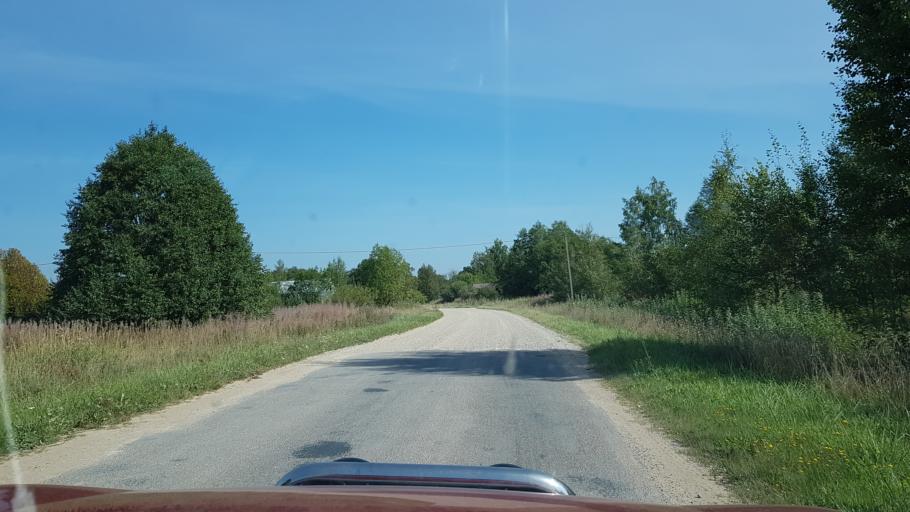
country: EE
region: Viljandimaa
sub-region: Vohma linn
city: Vohma
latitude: 58.5233
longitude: 25.6591
